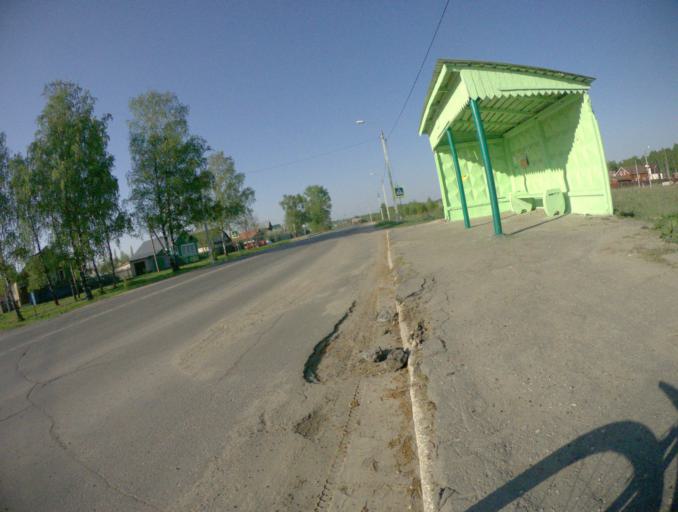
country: RU
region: Vladimir
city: Novovyazniki
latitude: 56.2245
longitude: 42.1883
